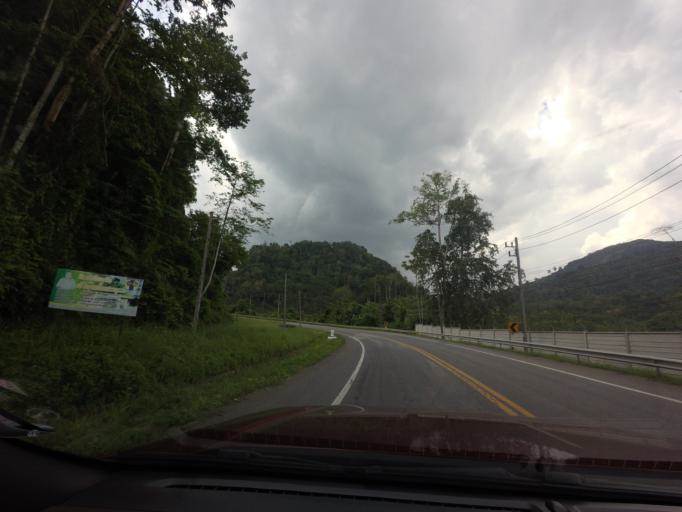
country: TH
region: Yala
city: Than To
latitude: 6.2010
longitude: 101.1740
